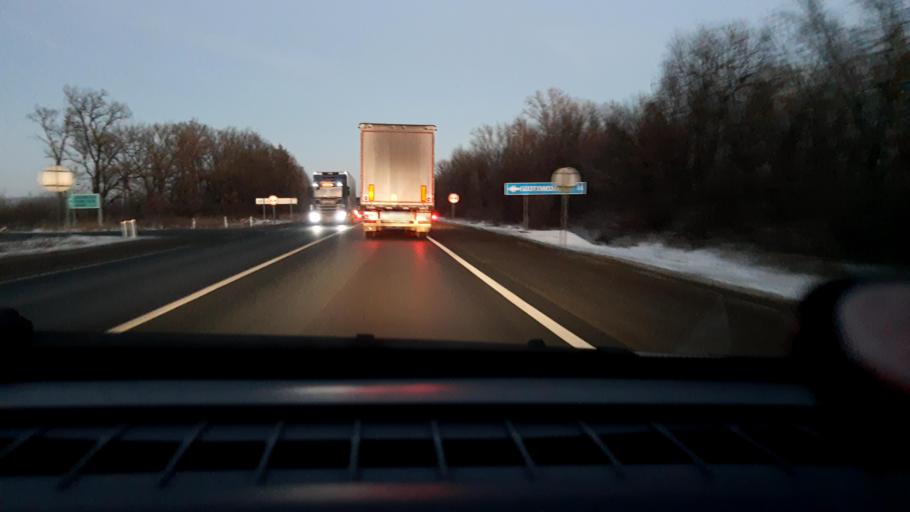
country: RU
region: Nizjnij Novgorod
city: Lyskovo
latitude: 56.0097
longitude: 44.9144
